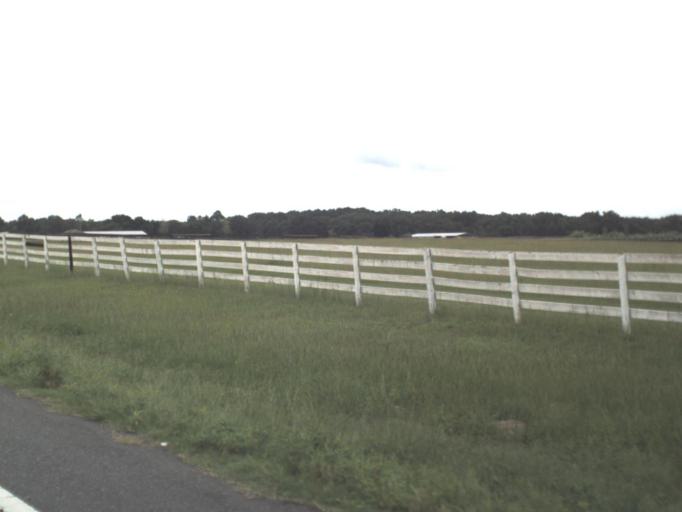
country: US
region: Florida
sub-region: Levy County
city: Williston
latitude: 29.3068
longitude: -82.4499
